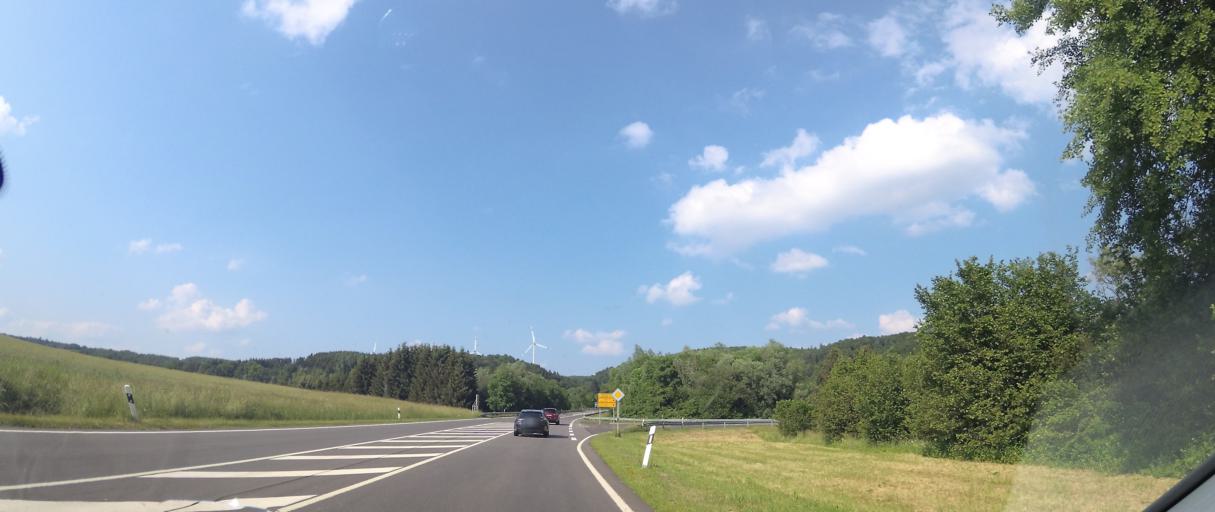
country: DE
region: Rheinland-Pfalz
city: Fohren-Linden
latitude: 49.5845
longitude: 7.2929
